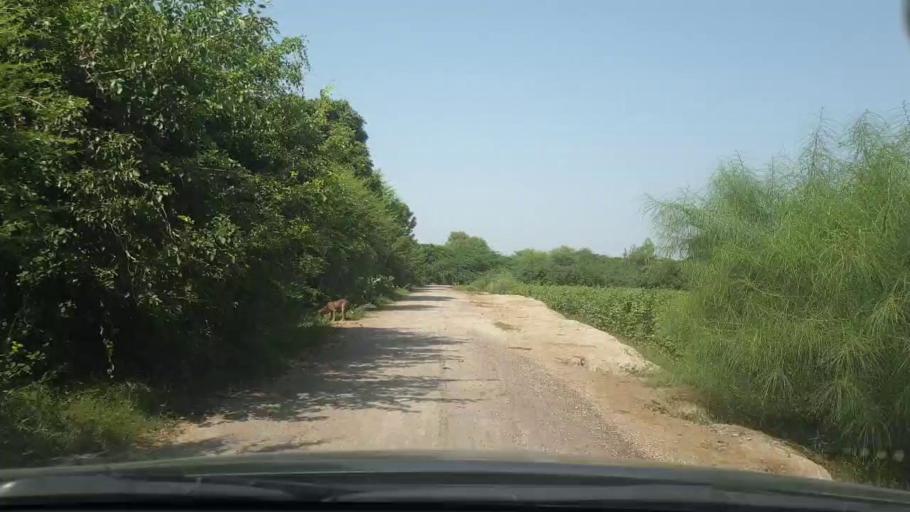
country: PK
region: Sindh
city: Naukot
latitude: 24.8165
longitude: 69.2621
